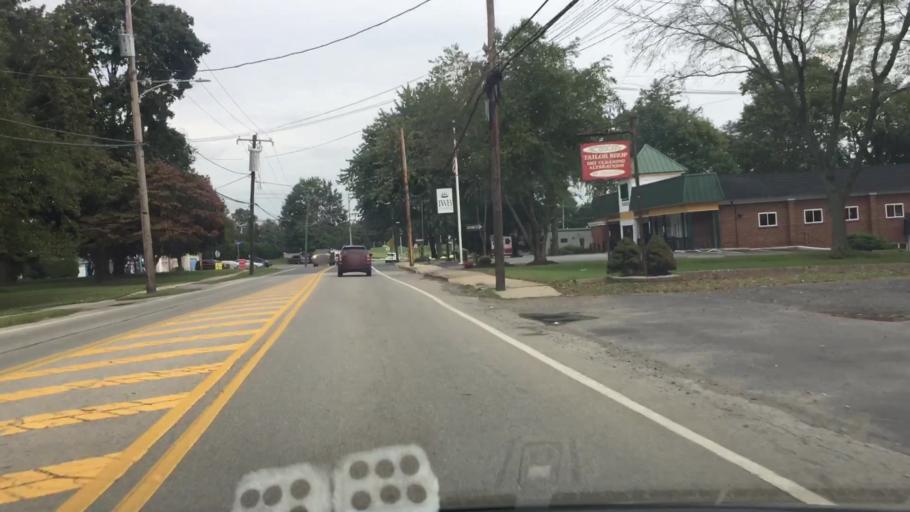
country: US
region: Pennsylvania
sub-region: Delaware County
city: Village Green-Green Ridge
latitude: 39.8669
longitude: -75.4230
